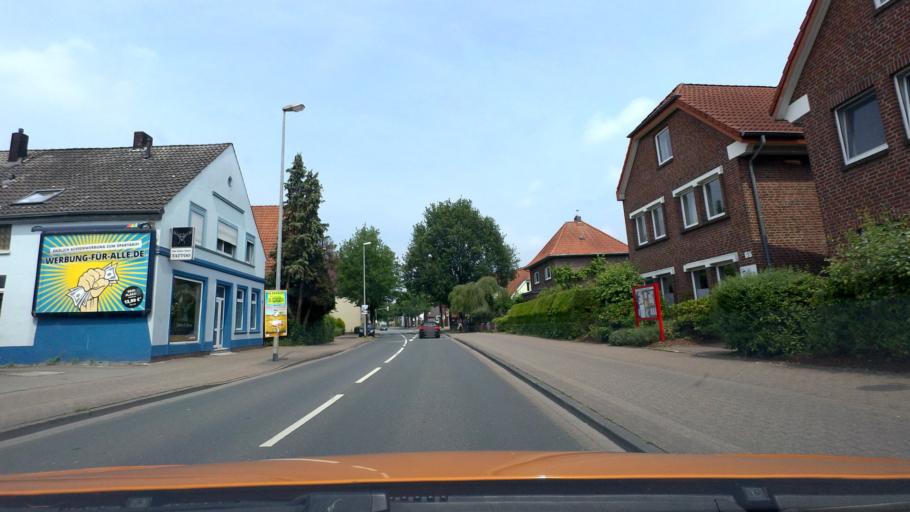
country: DE
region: Lower Saxony
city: Oldenburg
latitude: 53.1272
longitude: 8.2213
